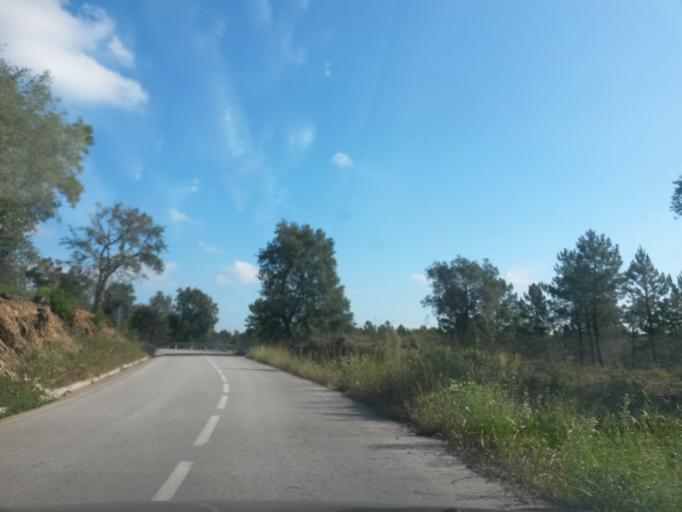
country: ES
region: Catalonia
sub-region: Provincia de Girona
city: Bescano
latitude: 41.9508
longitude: 2.6932
